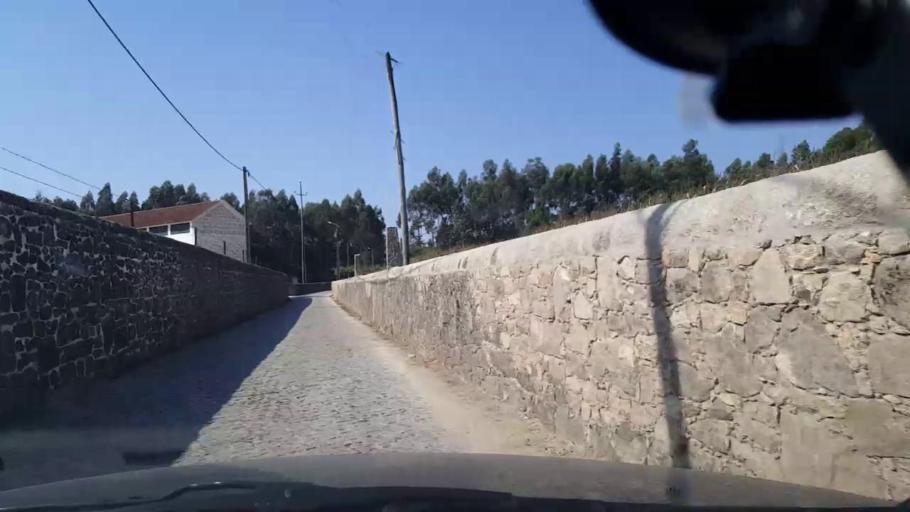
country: PT
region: Porto
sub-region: Povoa de Varzim
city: Pedroso
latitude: 41.3887
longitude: -8.7087
